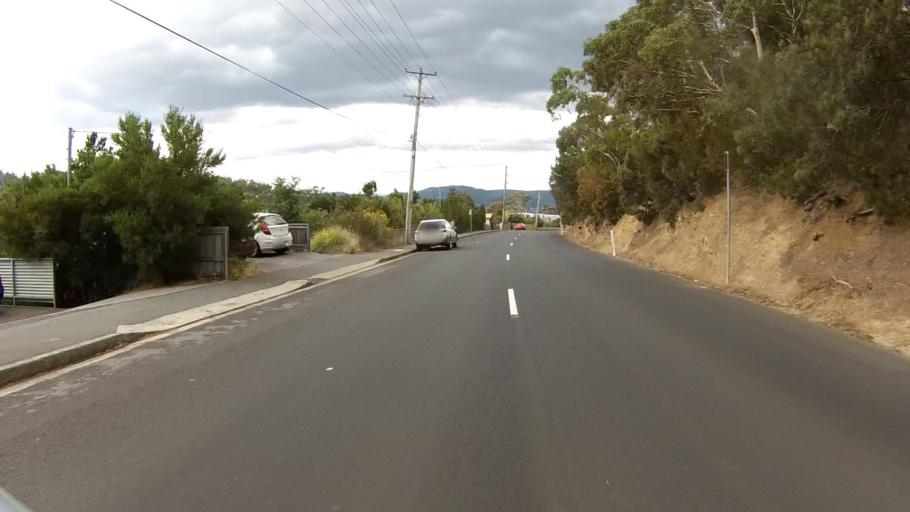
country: AU
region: Tasmania
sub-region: Hobart
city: Dynnyrne
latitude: -42.8990
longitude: 147.3001
